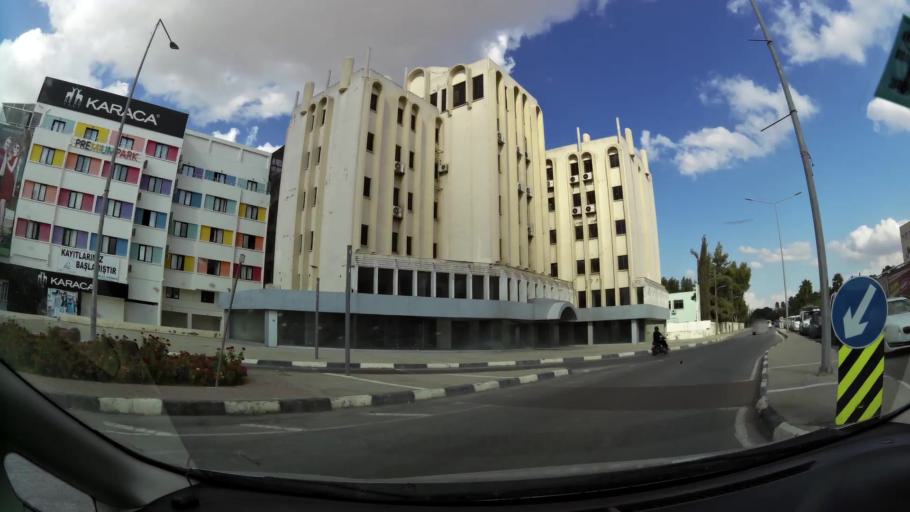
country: CY
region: Lefkosia
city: Nicosia
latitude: 35.1952
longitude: 33.3472
